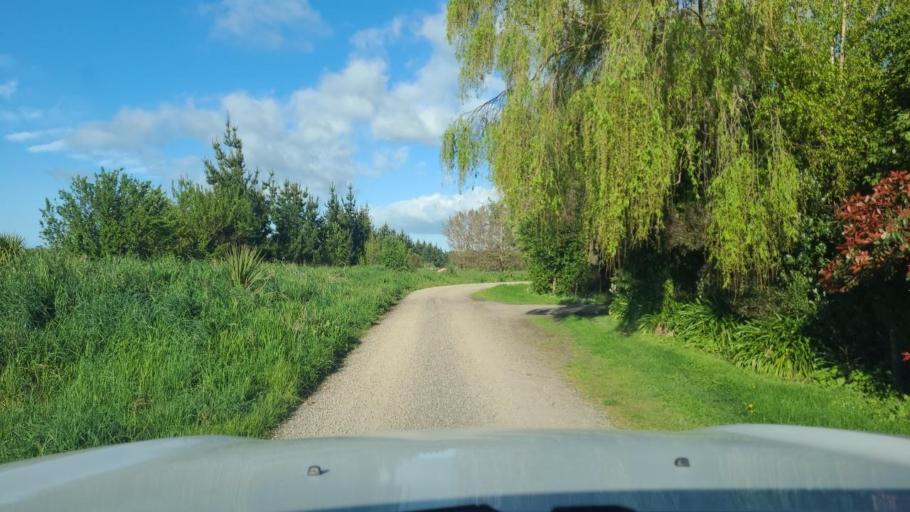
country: NZ
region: Wellington
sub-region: Upper Hutt City
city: Upper Hutt
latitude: -41.3009
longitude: 175.2611
